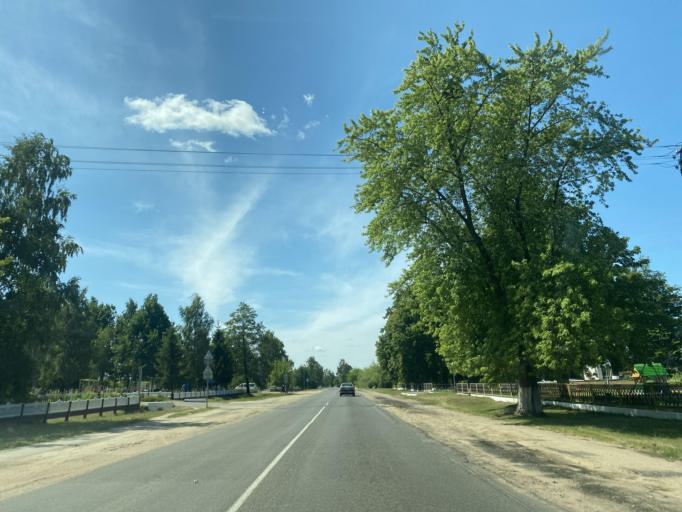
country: BY
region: Brest
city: Ivanava
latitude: 52.1666
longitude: 25.5495
